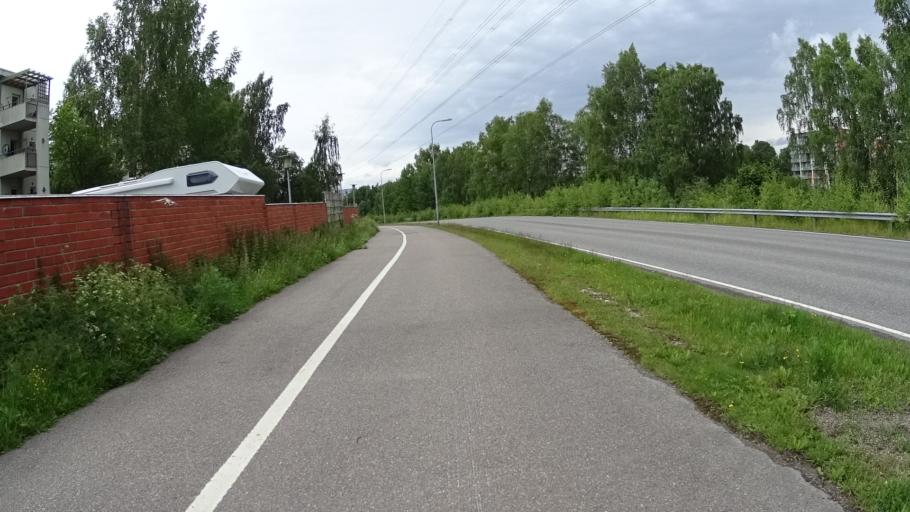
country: FI
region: Uusimaa
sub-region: Helsinki
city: Teekkarikylae
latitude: 60.2525
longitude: 24.8658
